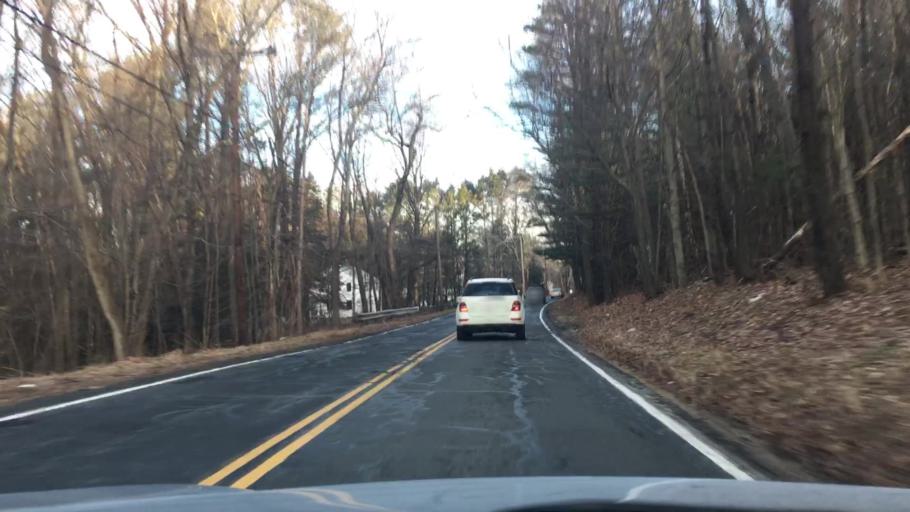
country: US
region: Massachusetts
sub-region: Hampden County
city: Southwick
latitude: 42.0724
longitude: -72.7234
